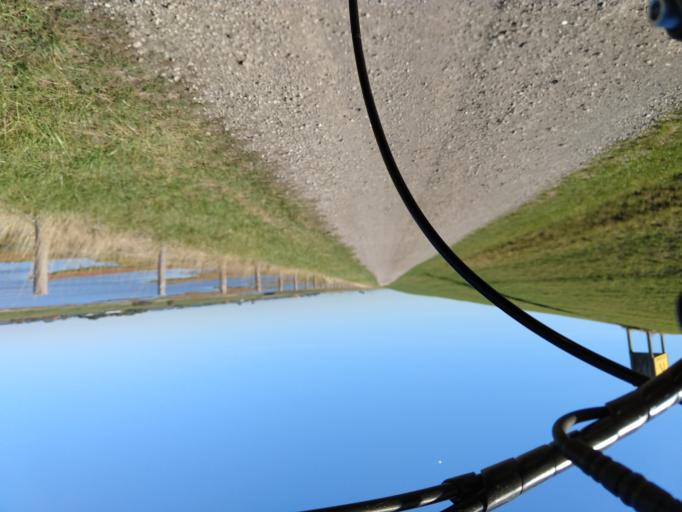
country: NL
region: Zeeland
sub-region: Gemeente Terneuzen
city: Terneuzen
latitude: 51.3910
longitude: 3.8060
